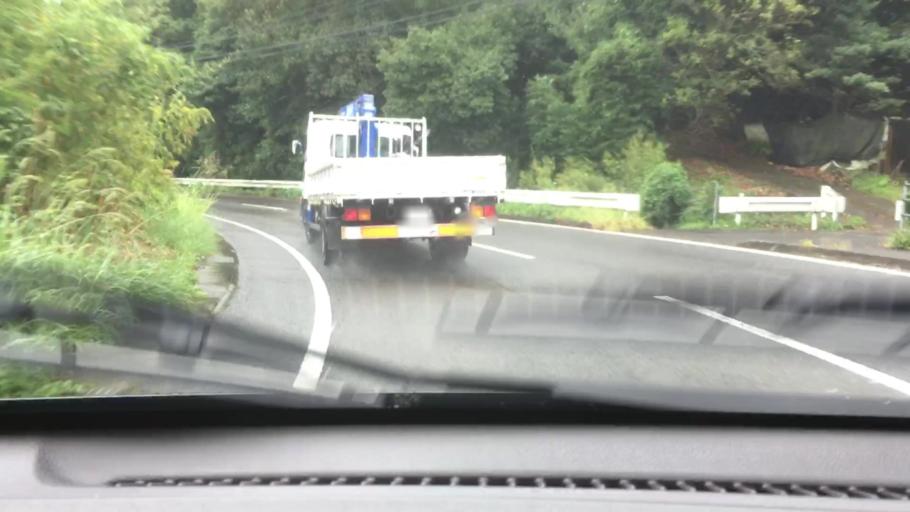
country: JP
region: Nagasaki
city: Togitsu
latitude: 32.8598
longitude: 129.7764
